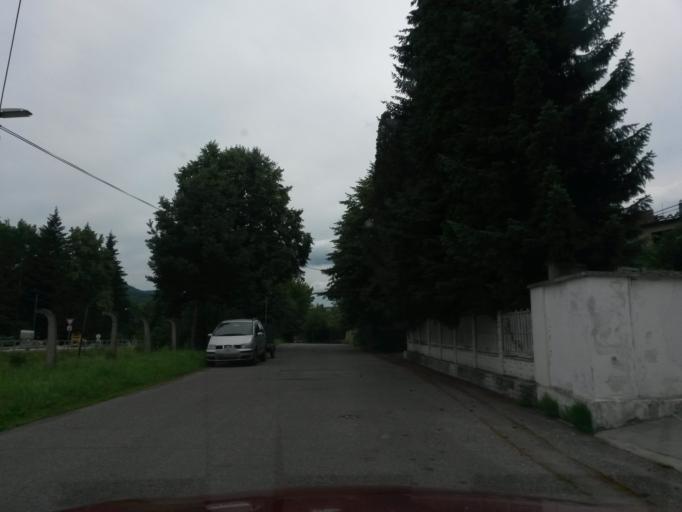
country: SK
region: Nitriansky
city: Handlova
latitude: 48.7312
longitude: 18.7548
